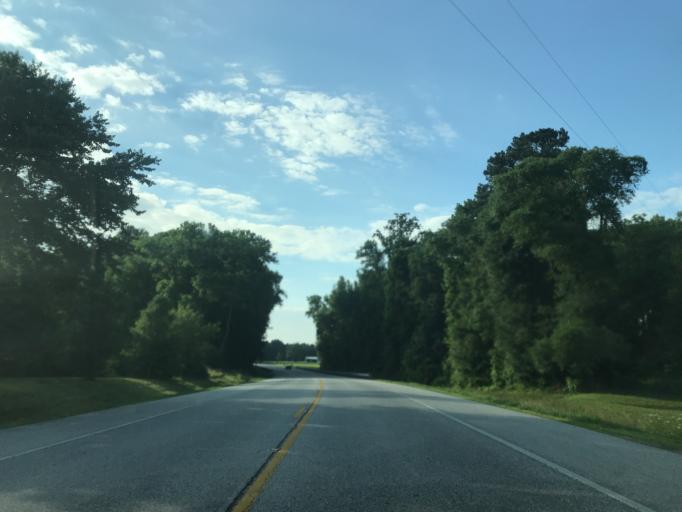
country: US
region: Maryland
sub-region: Caroline County
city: Federalsburg
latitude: 38.7293
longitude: -75.7869
